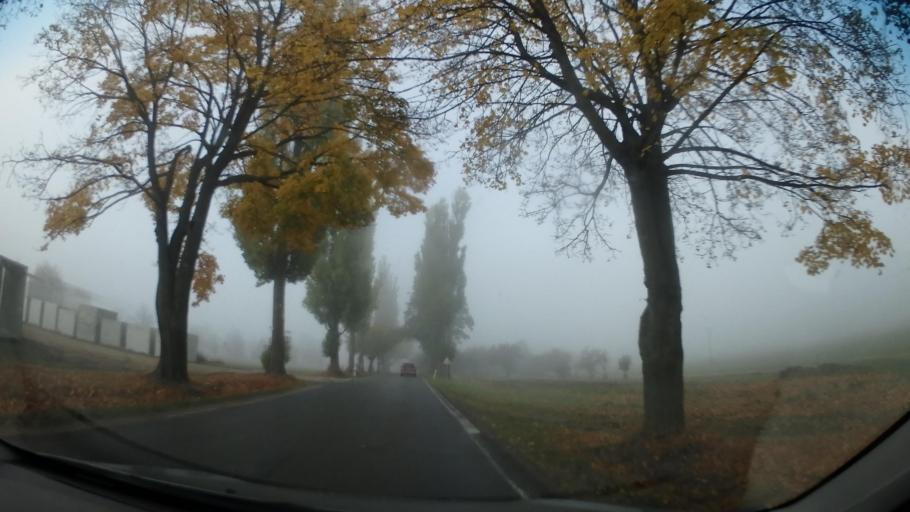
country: CZ
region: Vysocina
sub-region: Okres Zd'ar nad Sazavou
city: Nove Mesto na Morave
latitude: 49.4740
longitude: 16.0671
